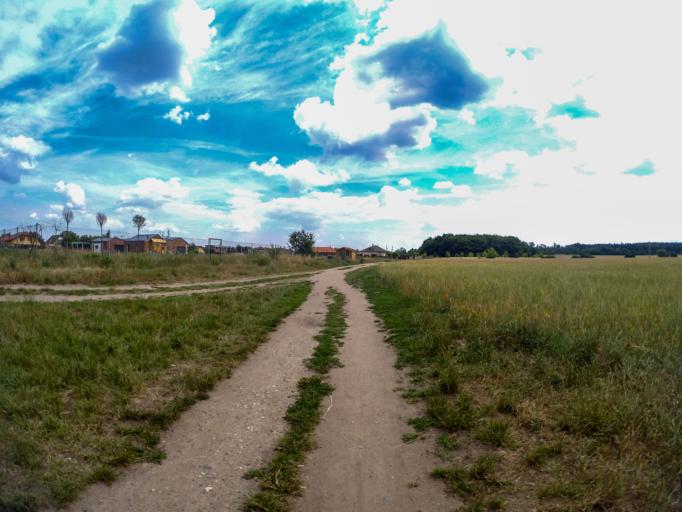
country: CZ
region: Central Bohemia
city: Neratovice
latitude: 50.2518
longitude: 14.5221
